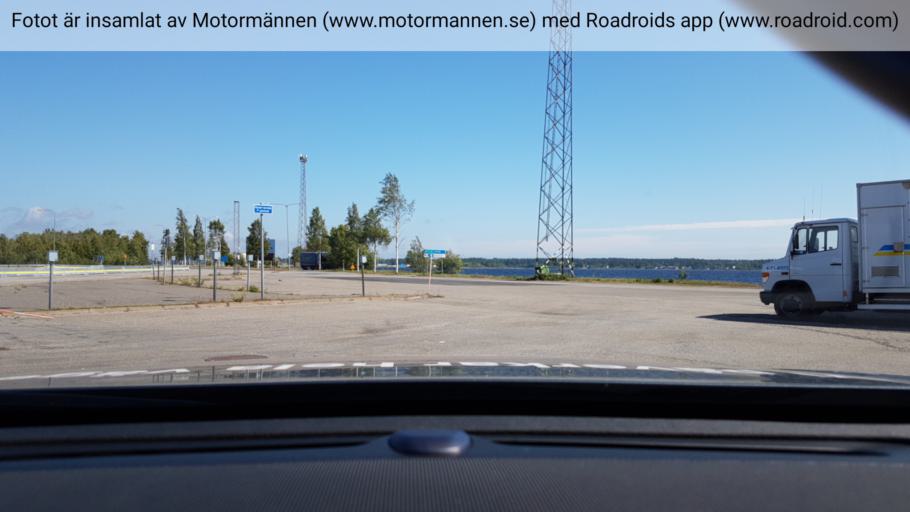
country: SE
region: Vaesterbotten
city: Obbola
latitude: 63.6834
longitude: 20.3393
